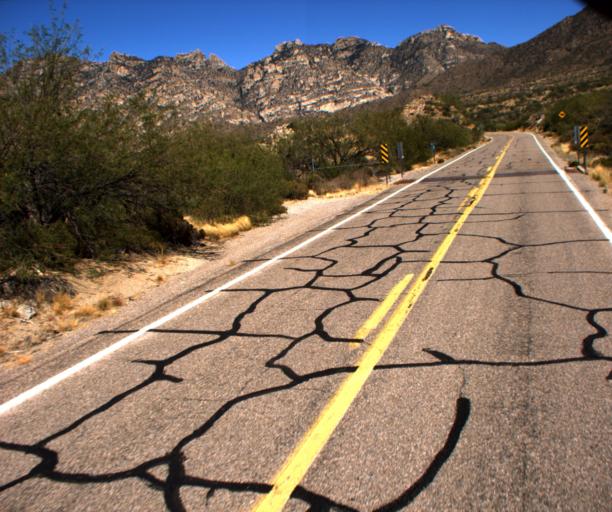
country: US
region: Arizona
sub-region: Pima County
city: Three Points
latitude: 31.9908
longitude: -111.5835
